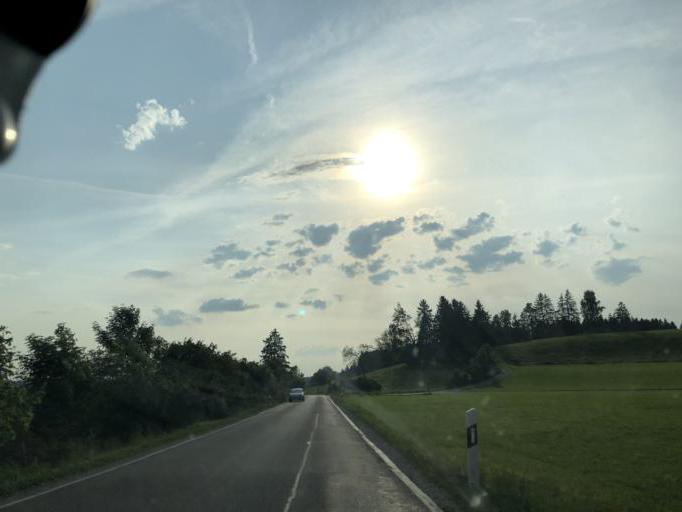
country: DE
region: Bavaria
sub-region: Swabia
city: Wald
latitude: 47.7567
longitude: 10.5573
